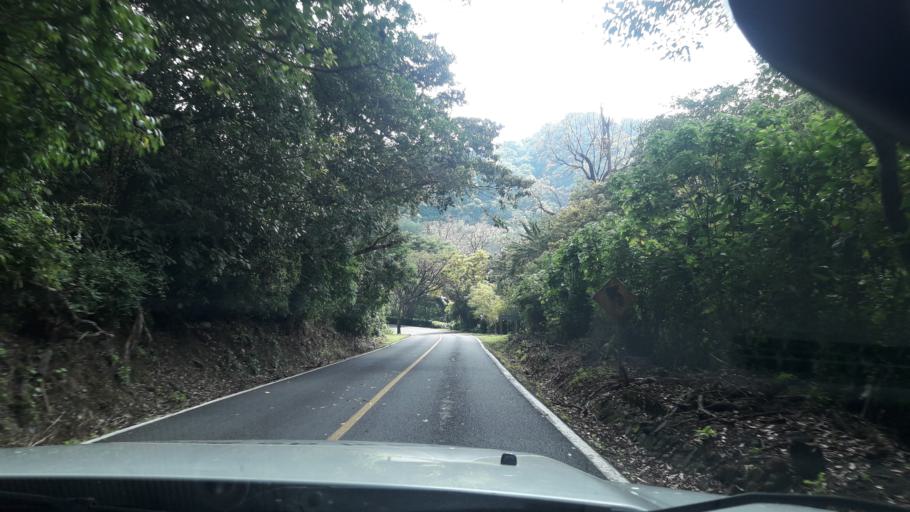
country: MX
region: Colima
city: Suchitlan
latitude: 19.4476
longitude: -103.7178
